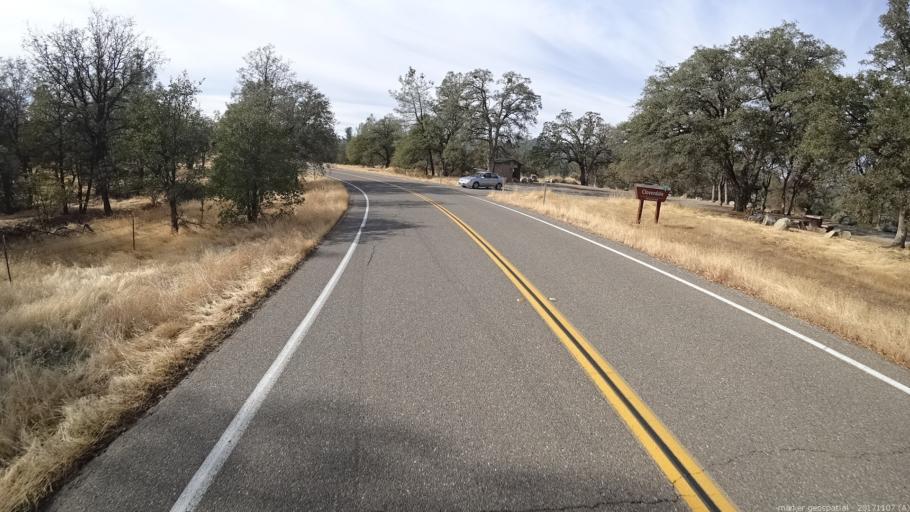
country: US
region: California
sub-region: Shasta County
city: Shasta
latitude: 40.5008
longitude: -122.5227
